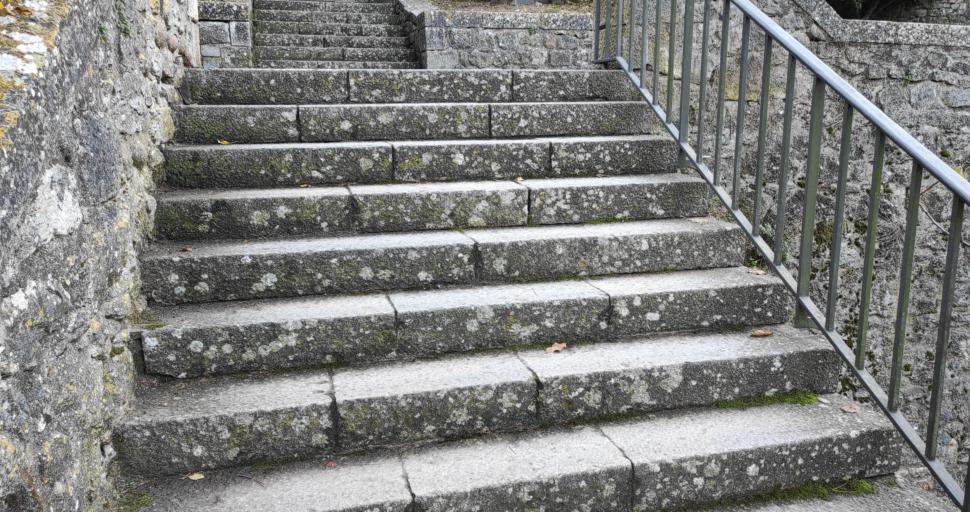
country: ES
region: Catalonia
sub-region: Provincia de Girona
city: Girona
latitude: 41.9880
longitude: 2.8265
